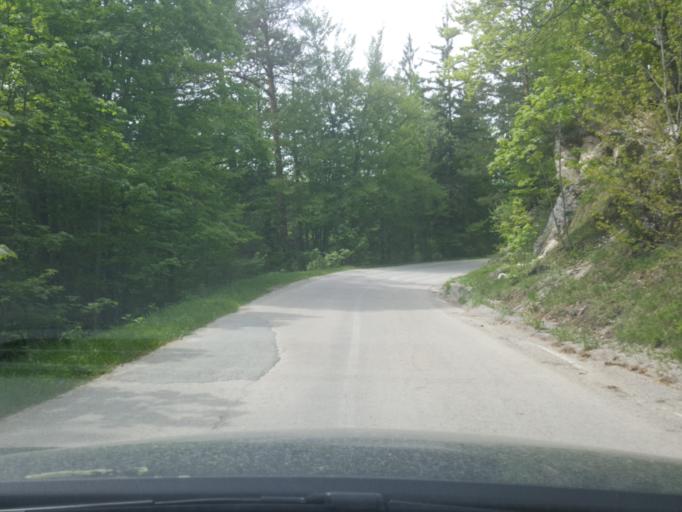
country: RS
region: Central Serbia
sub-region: Zlatiborski Okrug
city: Bajina Basta
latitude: 43.8896
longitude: 19.5268
